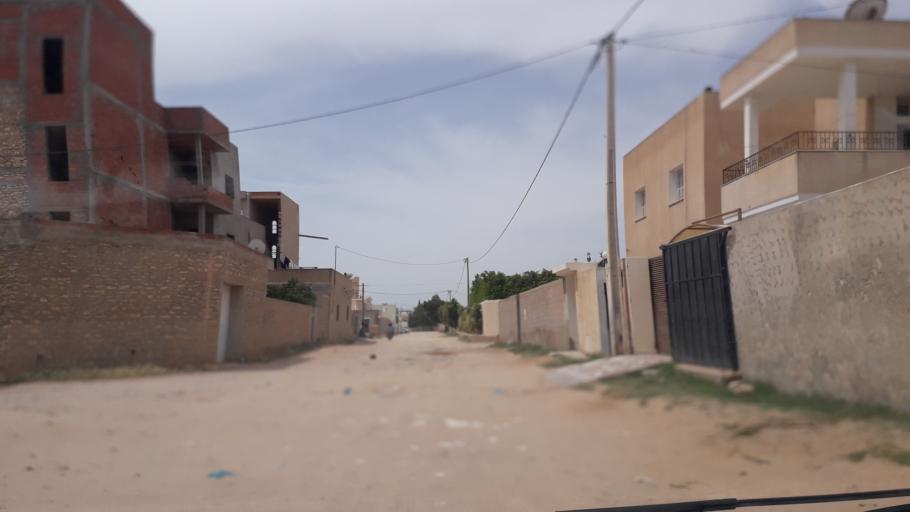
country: TN
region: Safaqis
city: Al Qarmadah
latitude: 34.8076
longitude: 10.7722
